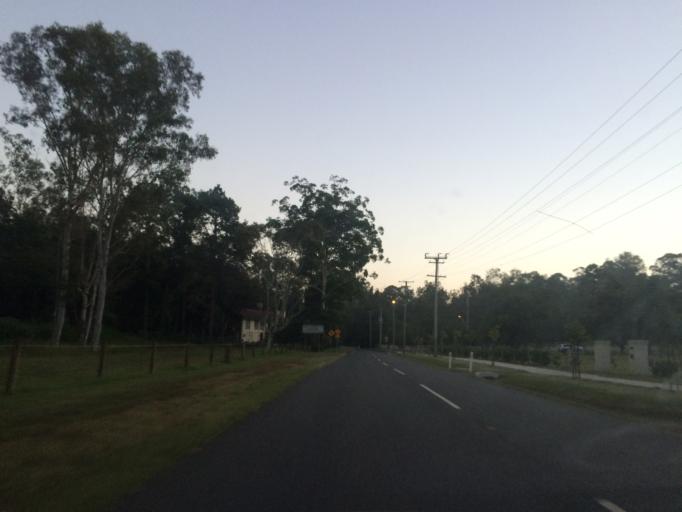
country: AU
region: Queensland
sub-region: Brisbane
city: Kenmore Hills
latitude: -27.5011
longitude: 152.9140
